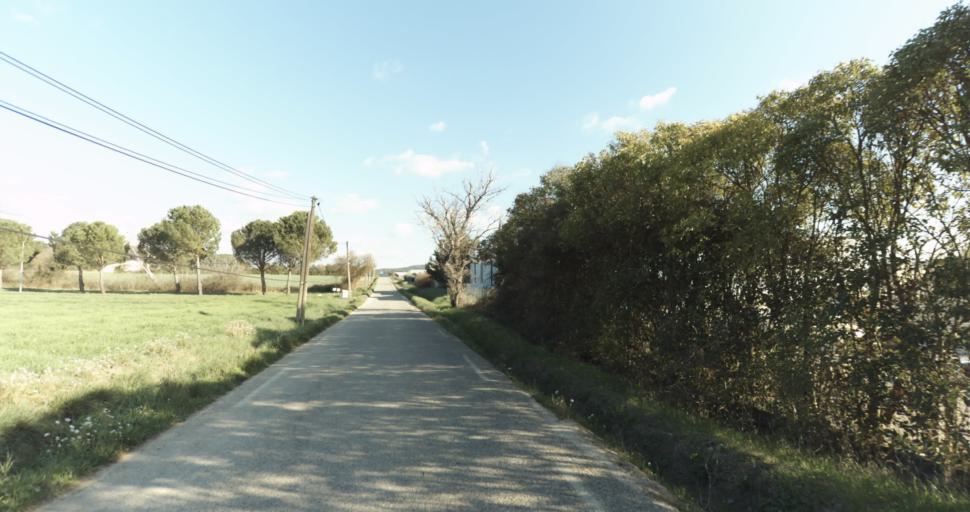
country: FR
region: Provence-Alpes-Cote d'Azur
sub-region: Departement des Bouches-du-Rhone
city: Bouc-Bel-Air
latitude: 43.4863
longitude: 5.3902
